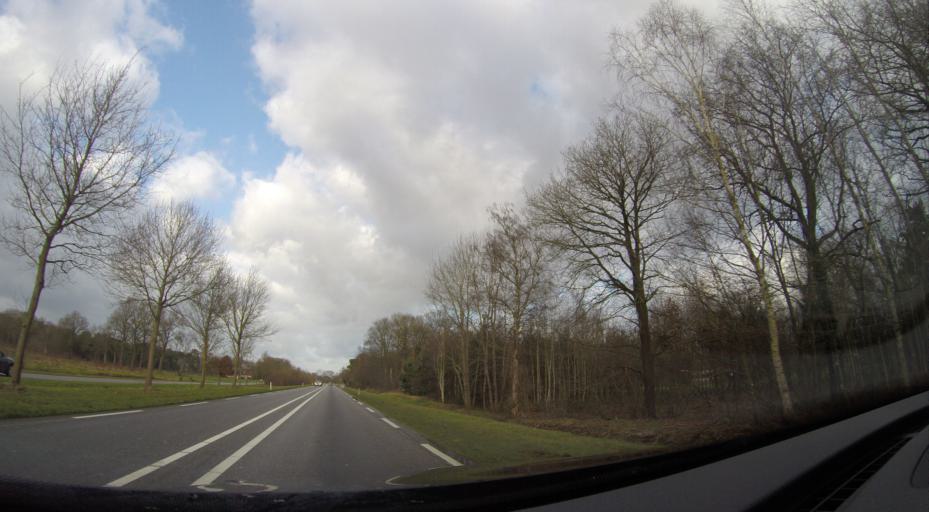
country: NL
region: Gelderland
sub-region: Gemeente Lochem
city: Lochem
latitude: 52.1524
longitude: 6.3904
